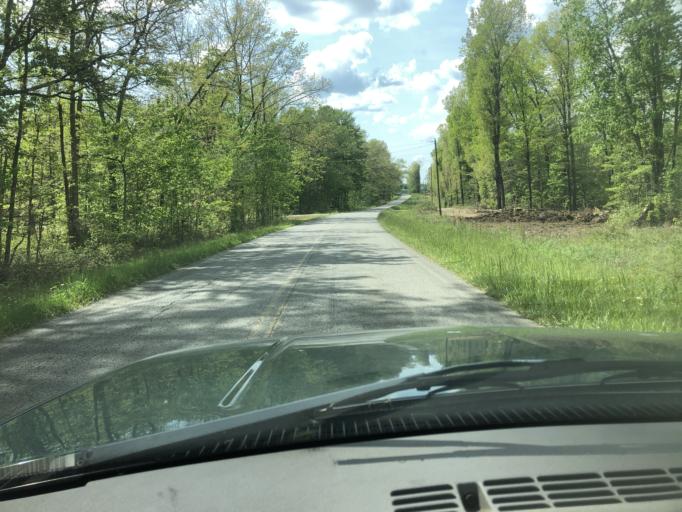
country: US
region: Tennessee
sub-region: Fentress County
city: Grimsley
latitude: 36.3123
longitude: -84.8532
